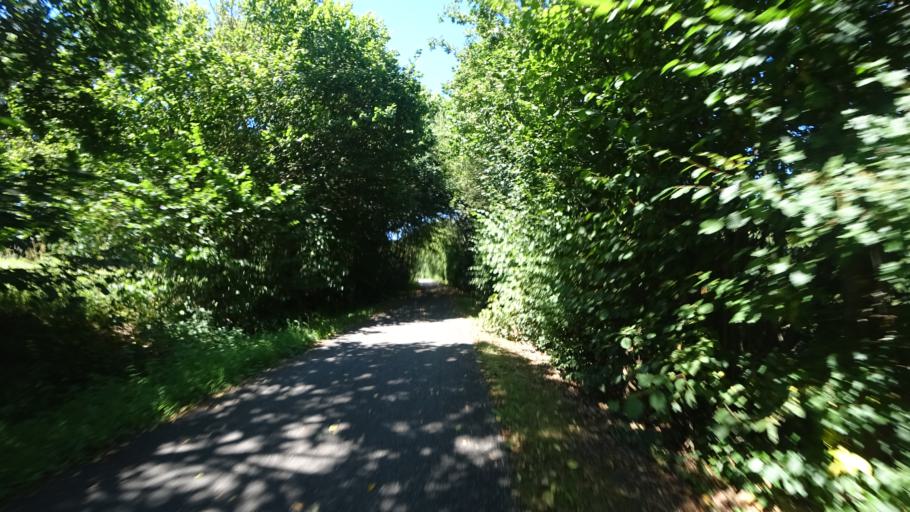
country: DE
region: Rheinland-Pfalz
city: Neuerkirch
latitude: 50.0195
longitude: 7.4833
